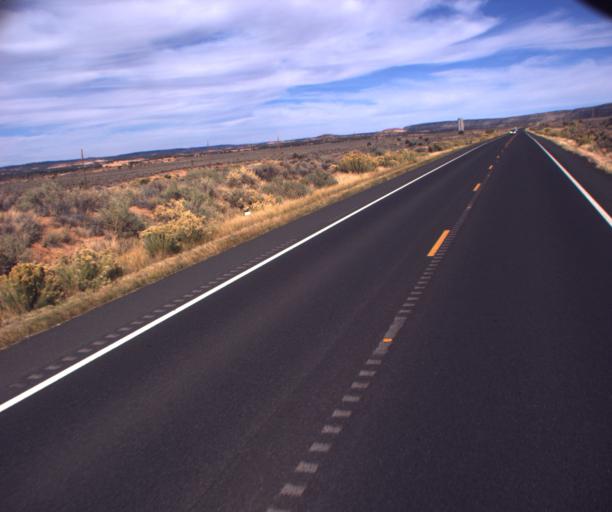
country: US
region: Arizona
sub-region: Navajo County
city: Kayenta
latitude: 36.5390
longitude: -110.5518
